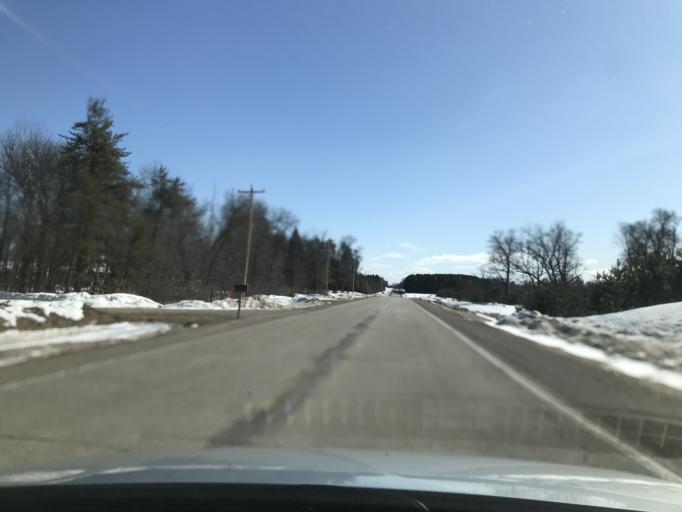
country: US
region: Wisconsin
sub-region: Marinette County
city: Niagara
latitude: 45.3528
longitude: -88.1012
